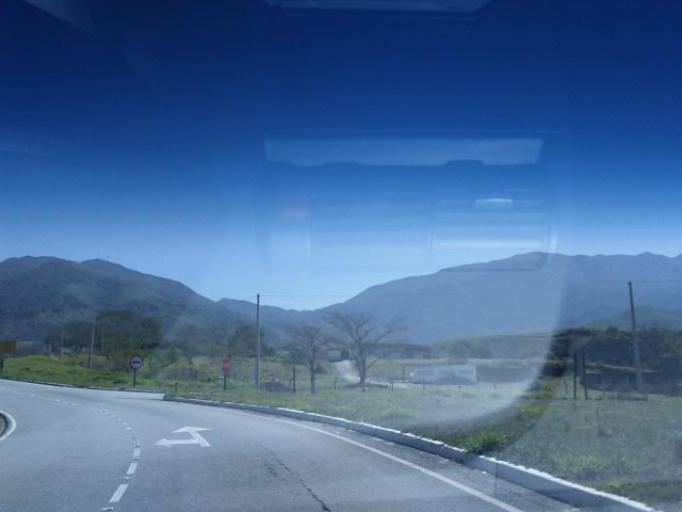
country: BR
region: Sao Paulo
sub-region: Tremembe
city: Tremembe
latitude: -22.8667
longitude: -45.5963
